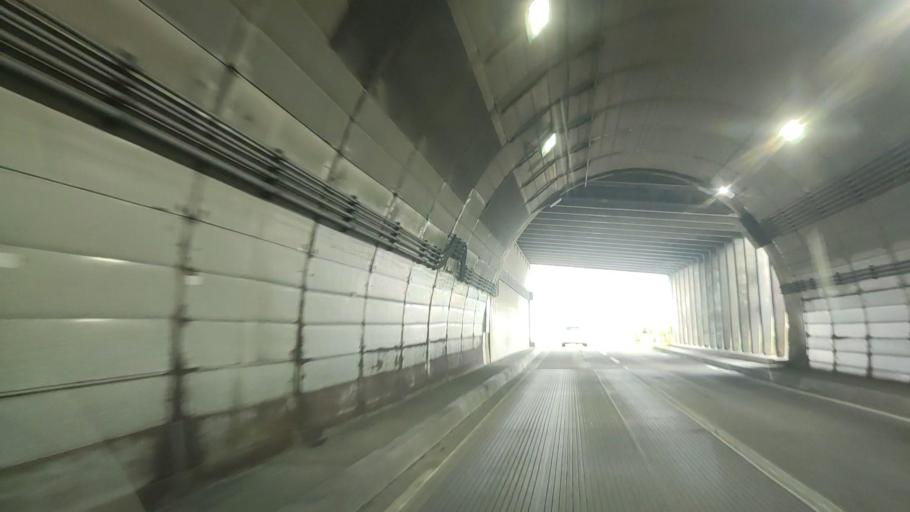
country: JP
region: Hokkaido
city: Ishikari
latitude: 43.4387
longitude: 141.4160
